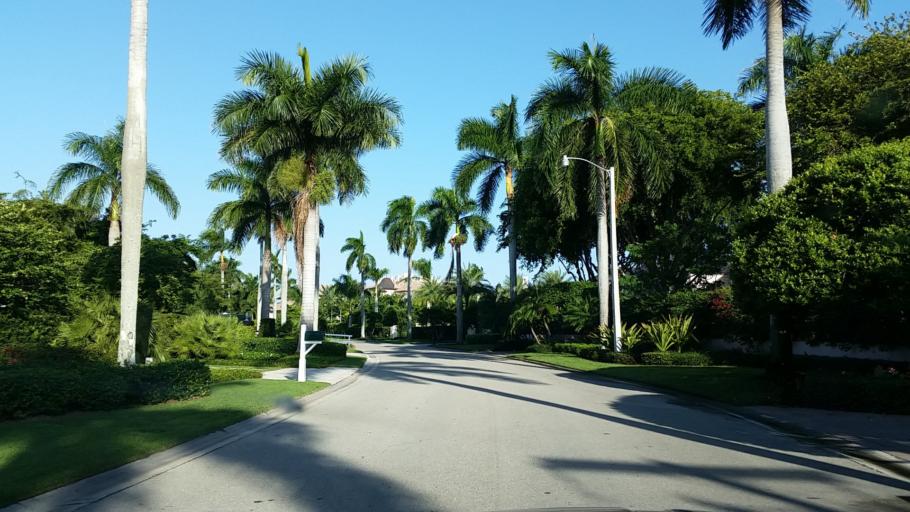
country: US
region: Florida
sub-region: Collier County
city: Naples
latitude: 26.1110
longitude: -81.7978
